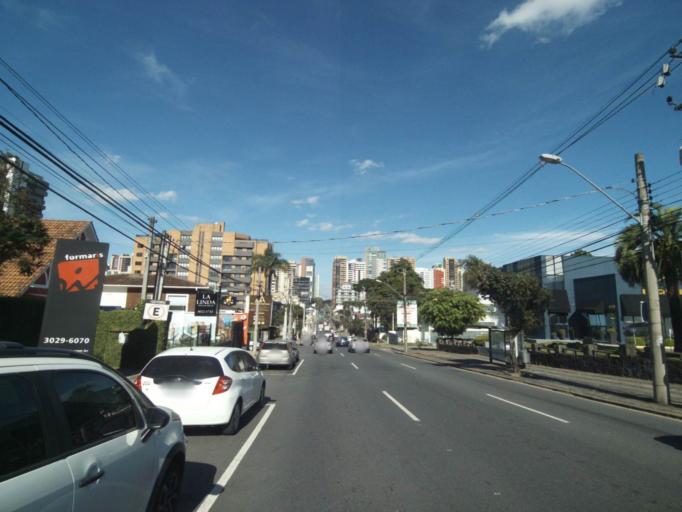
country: BR
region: Parana
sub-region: Curitiba
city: Curitiba
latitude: -25.4404
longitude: -49.2904
